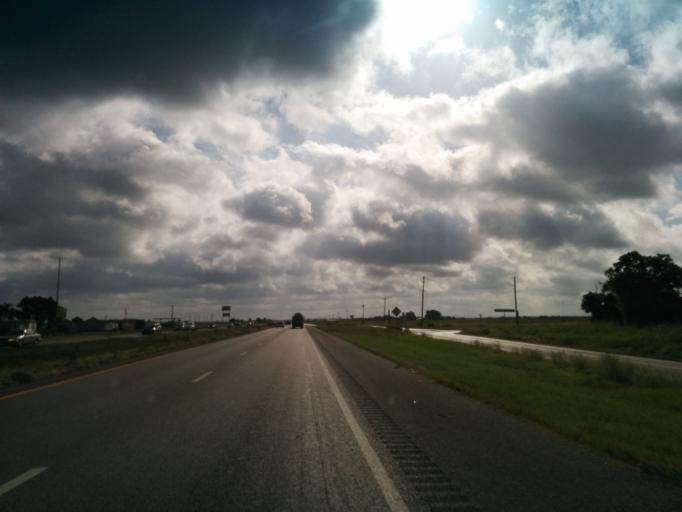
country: US
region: Texas
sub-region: Guadalupe County
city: Marion
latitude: 29.5190
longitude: -98.1387
